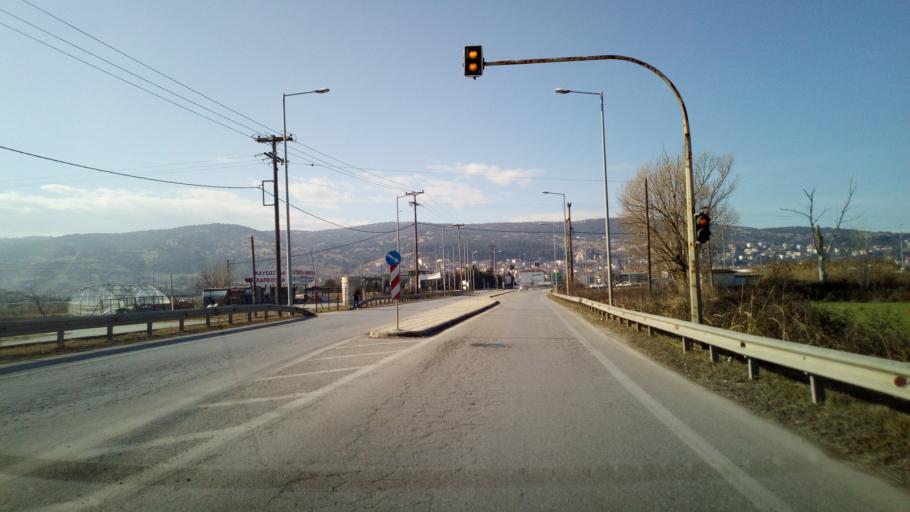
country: GR
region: Central Macedonia
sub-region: Nomos Thessalonikis
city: Lagyna
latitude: 40.7292
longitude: 23.0160
